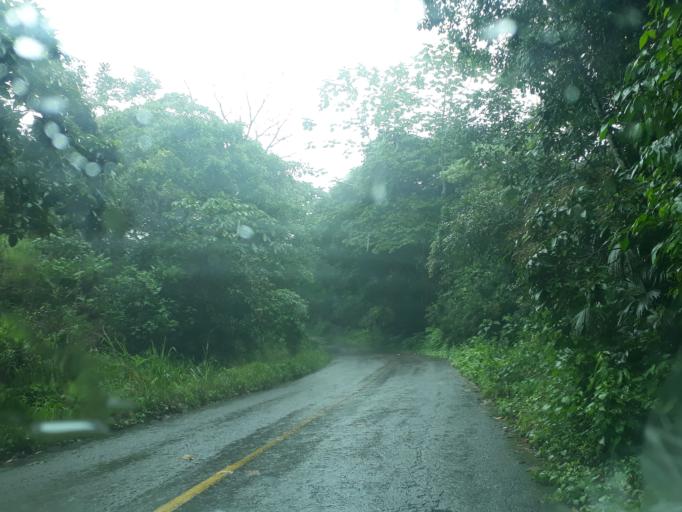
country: CO
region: Cundinamarca
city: Paratebueno
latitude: 4.4043
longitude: -73.3039
